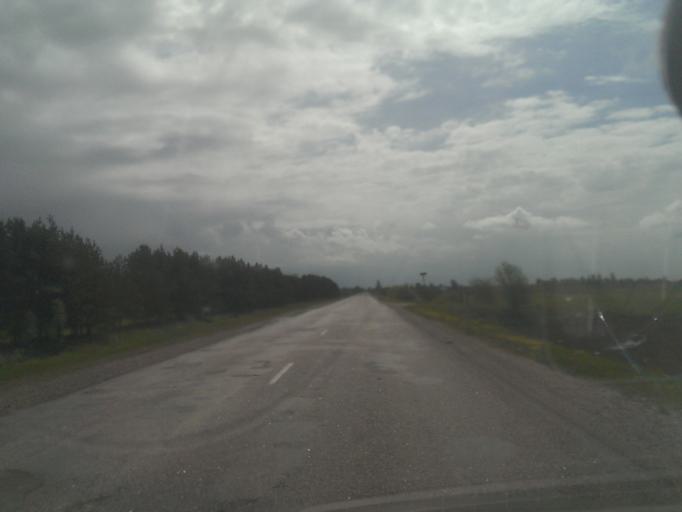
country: LV
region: Ventspils Rajons
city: Piltene
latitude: 57.2593
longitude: 21.5883
